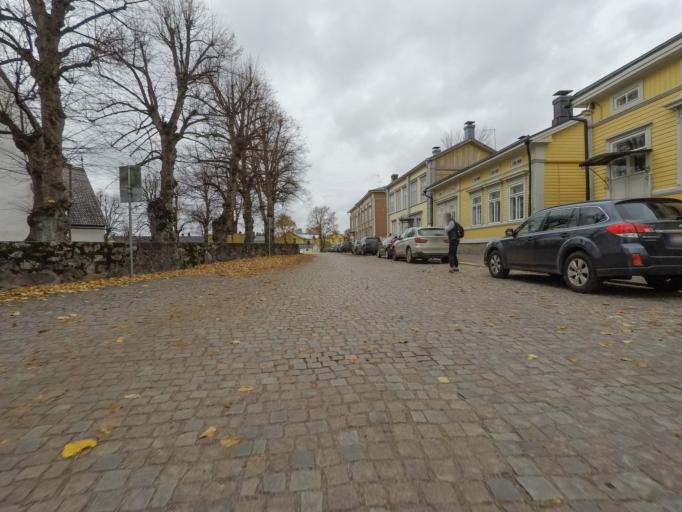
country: FI
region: Uusimaa
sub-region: Porvoo
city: Porvoo
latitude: 60.3972
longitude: 25.6588
